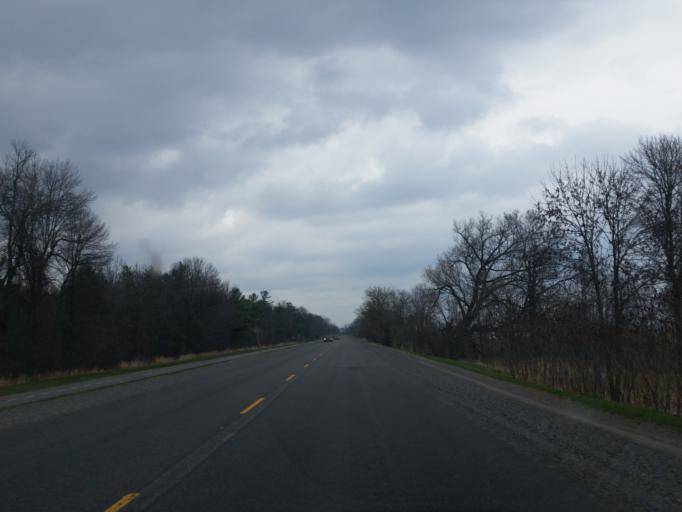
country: US
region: New York
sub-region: Jefferson County
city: Alexandria Bay
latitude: 44.4660
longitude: -75.8449
